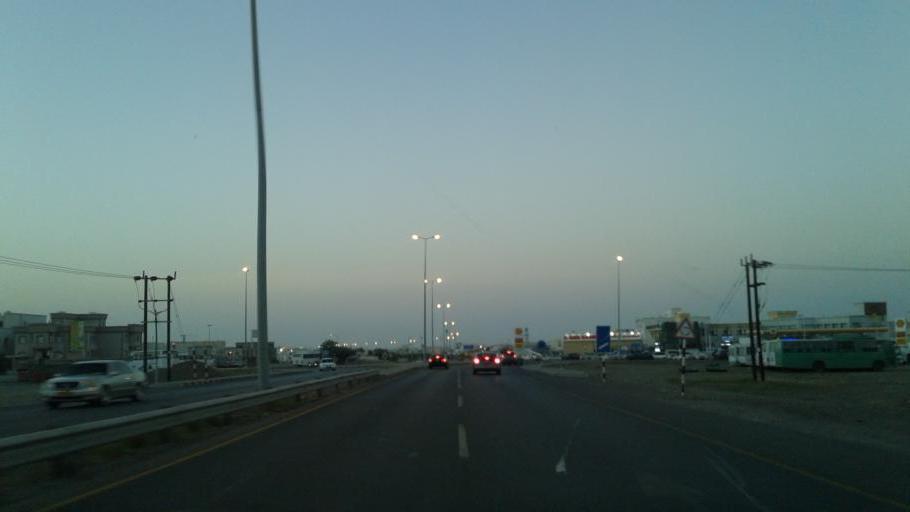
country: OM
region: Muhafazat Masqat
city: As Sib al Jadidah
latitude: 23.6003
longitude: 58.2174
